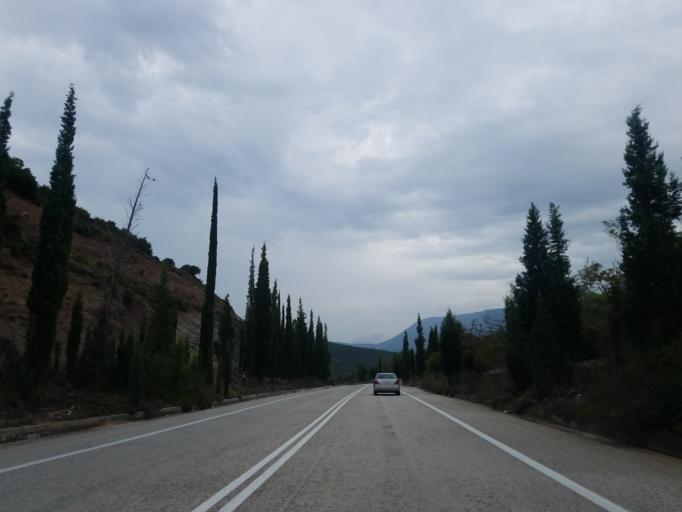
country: GR
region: Central Greece
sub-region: Nomos Voiotias
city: Livadeia
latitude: 38.4427
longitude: 22.8072
